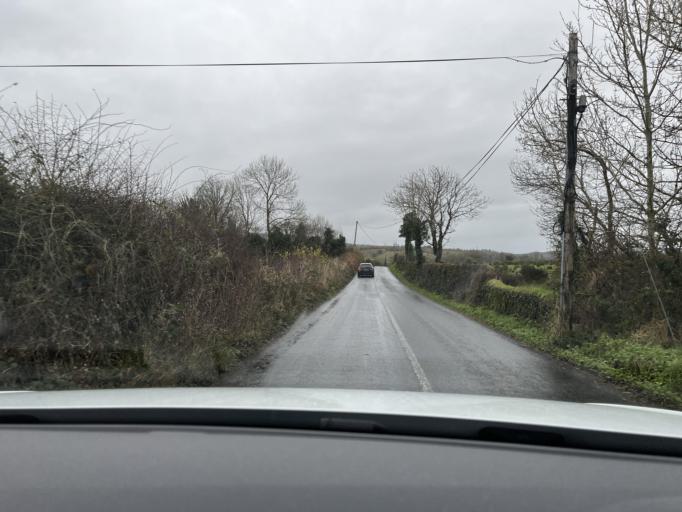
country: IE
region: Connaught
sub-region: County Leitrim
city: Manorhamilton
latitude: 54.2584
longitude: -8.2425
